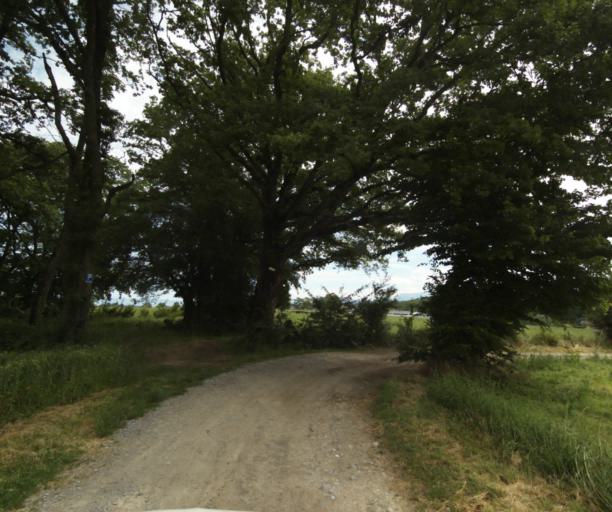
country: FR
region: Rhone-Alpes
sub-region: Departement de la Haute-Savoie
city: Margencel
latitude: 46.3443
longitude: 6.4310
